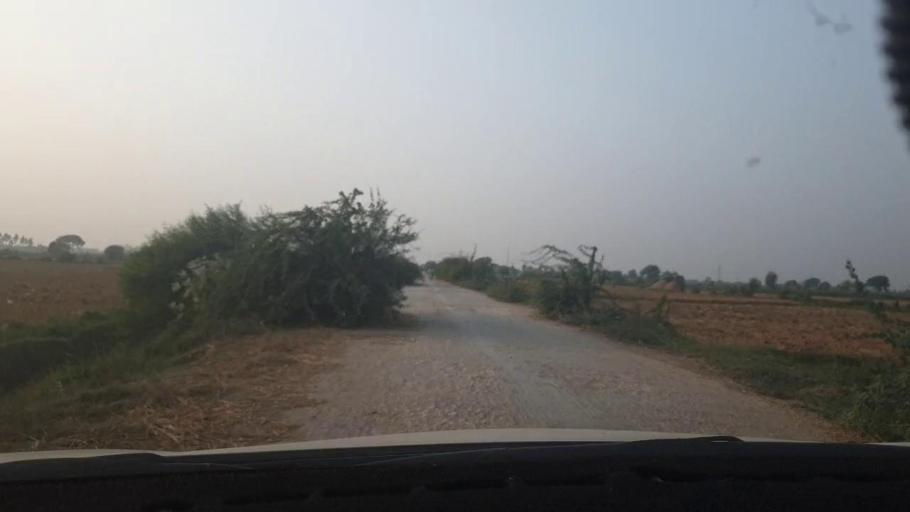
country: PK
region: Sindh
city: Bulri
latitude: 24.8515
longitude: 68.3430
